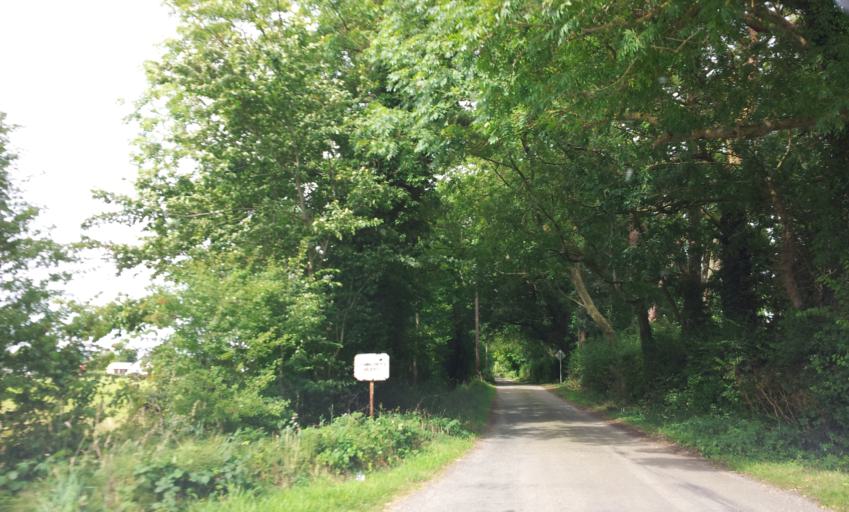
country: IE
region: Leinster
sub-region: Kildare
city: Moone
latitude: 52.9871
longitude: -6.8549
